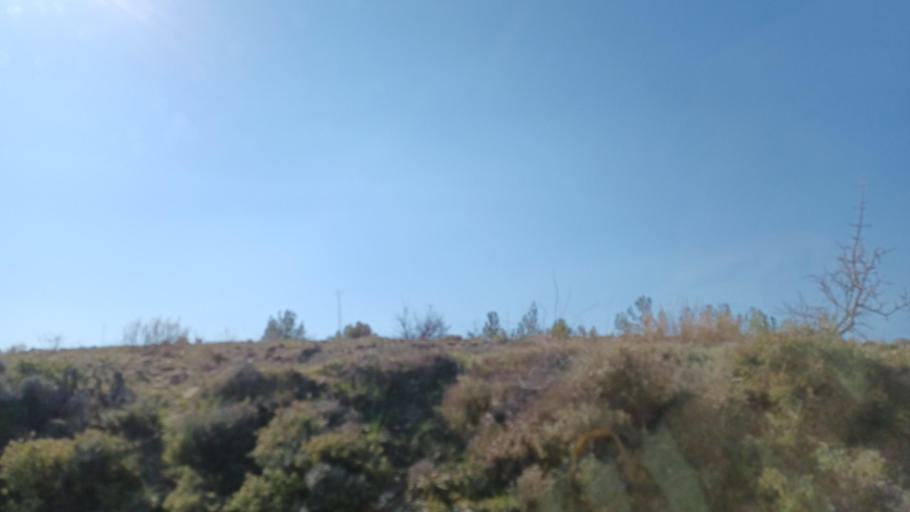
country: CY
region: Limassol
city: Pachna
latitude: 34.8488
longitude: 32.6900
